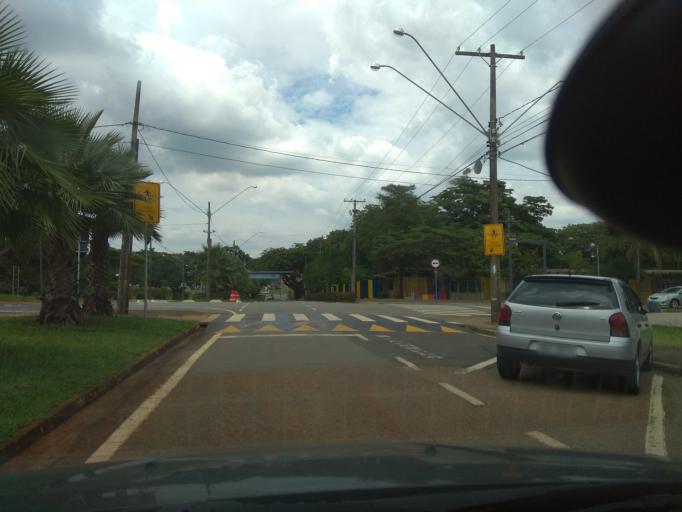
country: BR
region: Sao Paulo
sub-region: Campinas
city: Campinas
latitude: -22.8212
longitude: -47.0676
